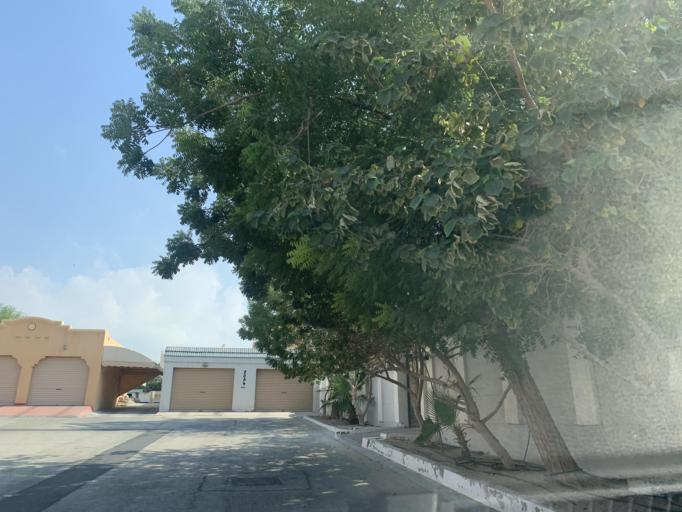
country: BH
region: Central Governorate
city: Madinat Hamad
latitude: 26.1059
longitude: 50.5013
